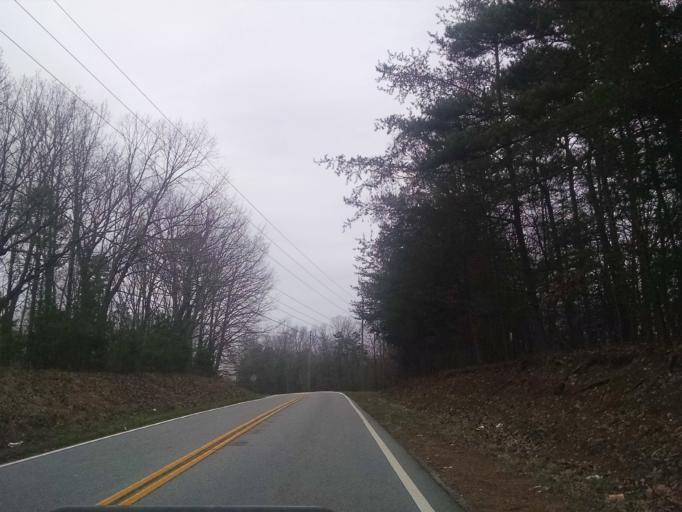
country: US
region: Georgia
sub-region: Hall County
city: Flowery Branch
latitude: 34.1857
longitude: -83.8991
